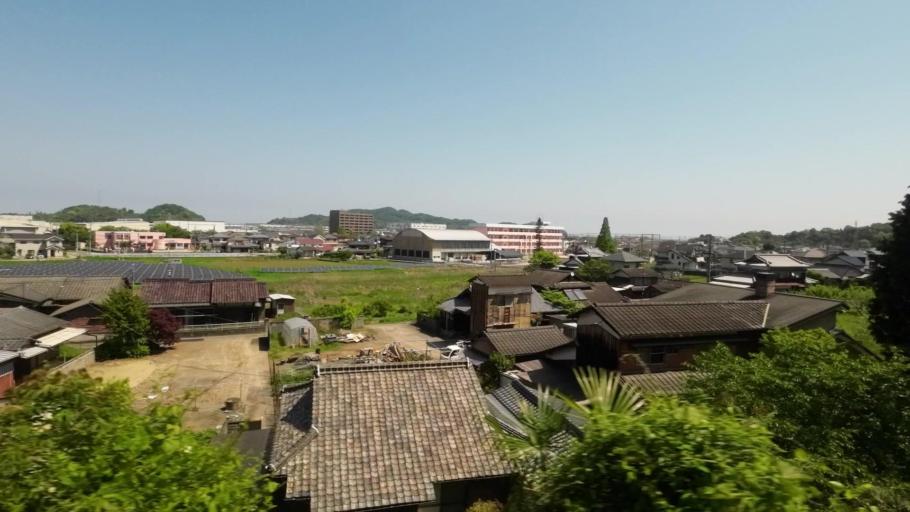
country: JP
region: Ehime
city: Niihama
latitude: 33.9725
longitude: 133.3499
